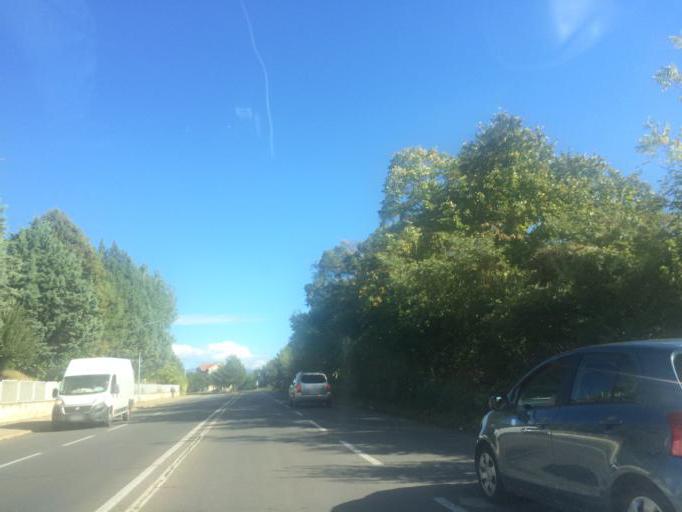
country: MK
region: Kocani
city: Orizari
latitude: 41.9135
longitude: 22.4348
